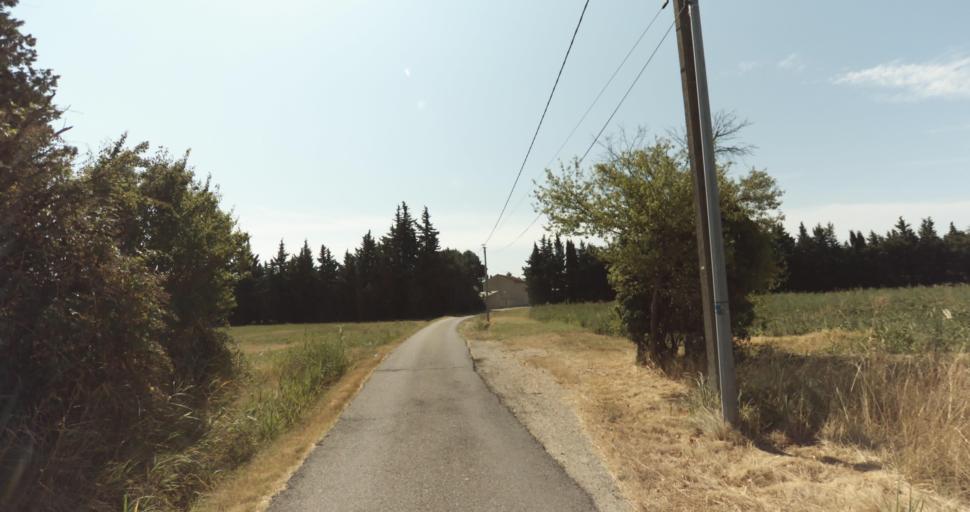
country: FR
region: Provence-Alpes-Cote d'Azur
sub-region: Departement du Vaucluse
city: Monteux
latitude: 44.0184
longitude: 4.9988
